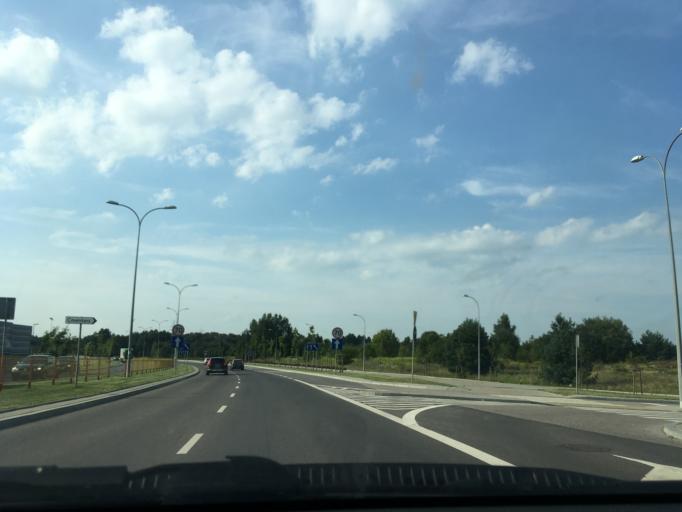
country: PL
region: Podlasie
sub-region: Bialystok
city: Bialystok
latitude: 53.1348
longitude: 23.2217
